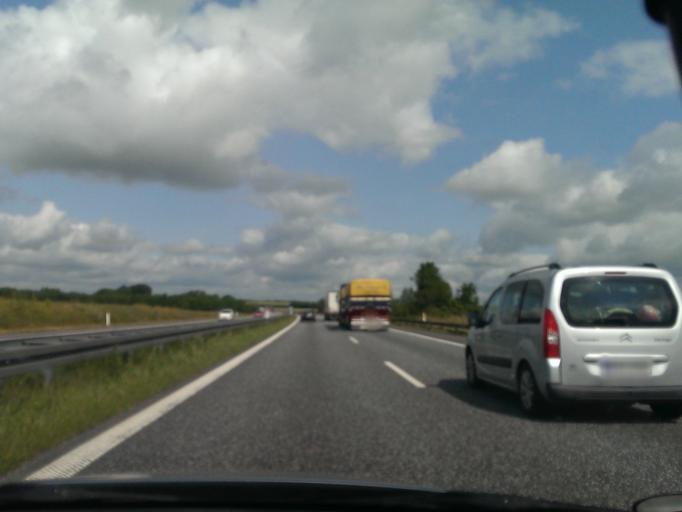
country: DK
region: Central Jutland
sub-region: Randers Kommune
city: Spentrup
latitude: 56.5082
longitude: 9.9722
